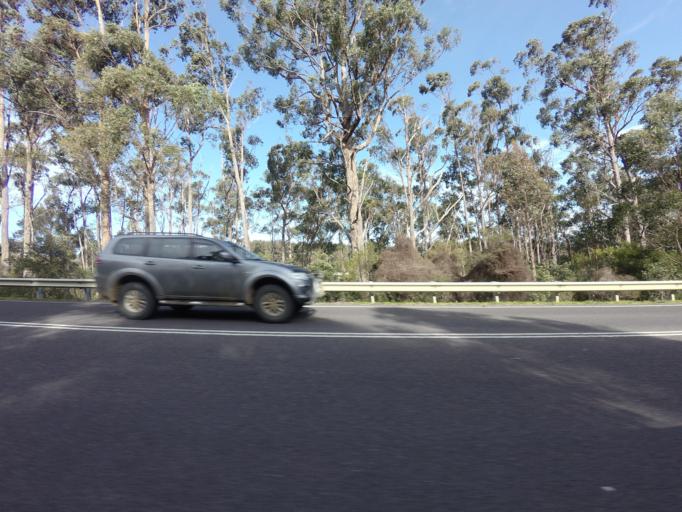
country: AU
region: Tasmania
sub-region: Huon Valley
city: Cygnet
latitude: -43.1218
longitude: 147.0420
